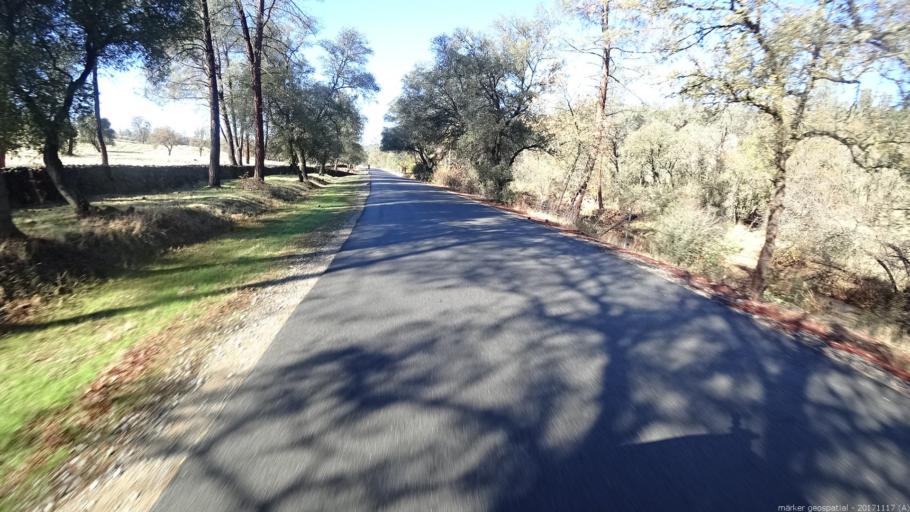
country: US
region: California
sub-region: Shasta County
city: Cottonwood
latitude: 40.4414
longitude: -122.1420
